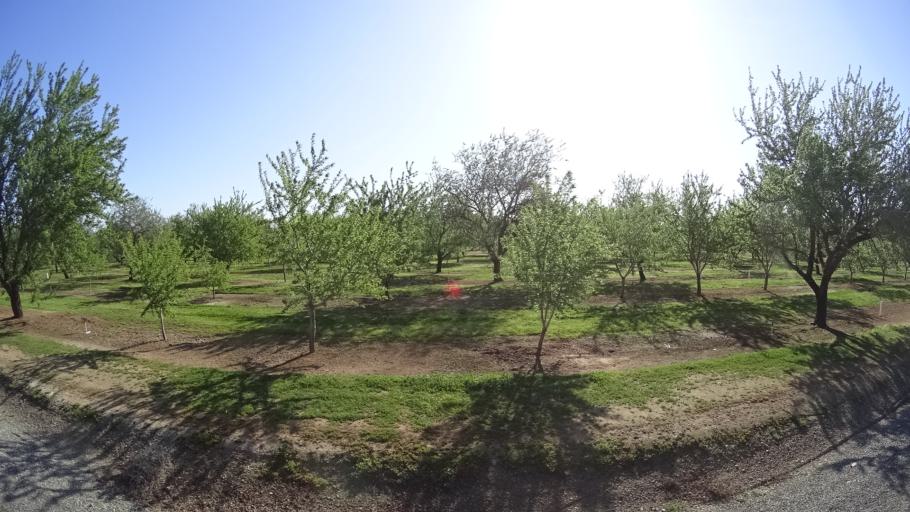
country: US
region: California
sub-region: Glenn County
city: Hamilton City
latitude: 39.7690
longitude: -122.1041
